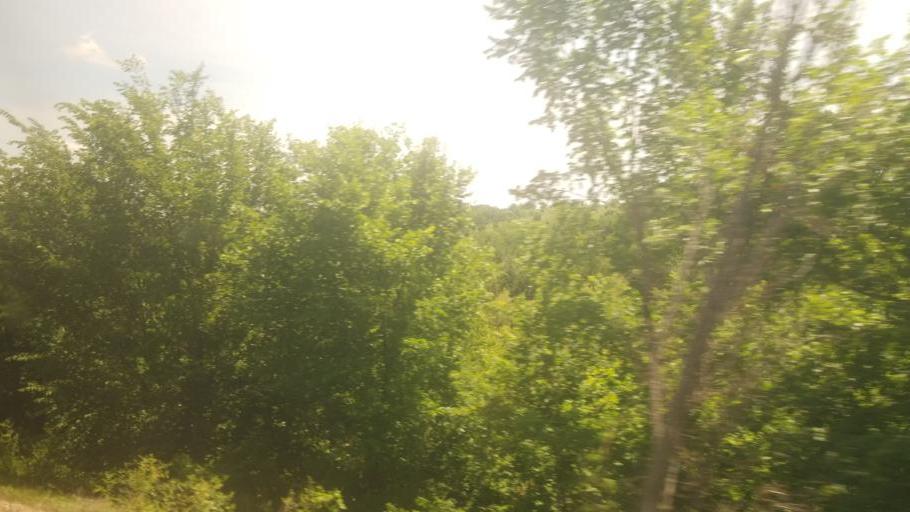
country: US
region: Missouri
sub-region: Linn County
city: Marceline
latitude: 39.8638
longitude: -92.8000
